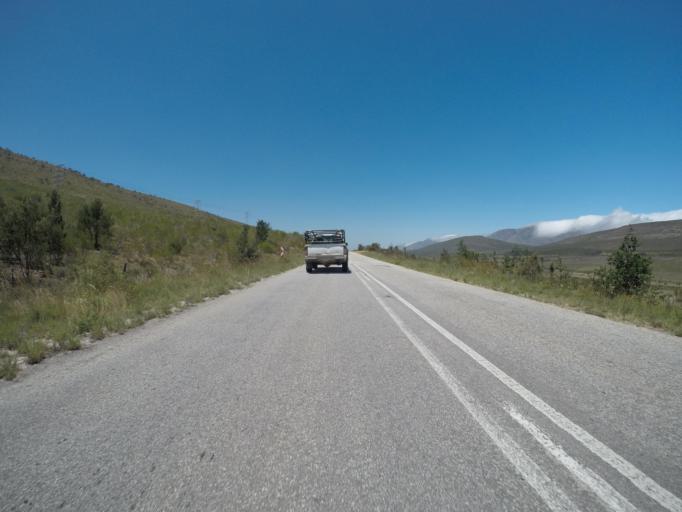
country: ZA
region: Eastern Cape
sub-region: Cacadu District Municipality
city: Kareedouw
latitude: -33.8412
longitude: 23.9348
